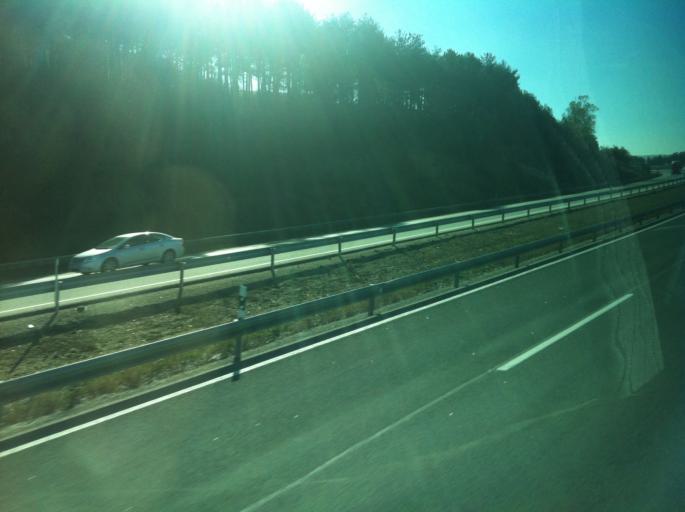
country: ES
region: Castille and Leon
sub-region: Provincia de Burgos
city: Fresno de Rodilla
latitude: 42.4384
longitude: -3.4962
